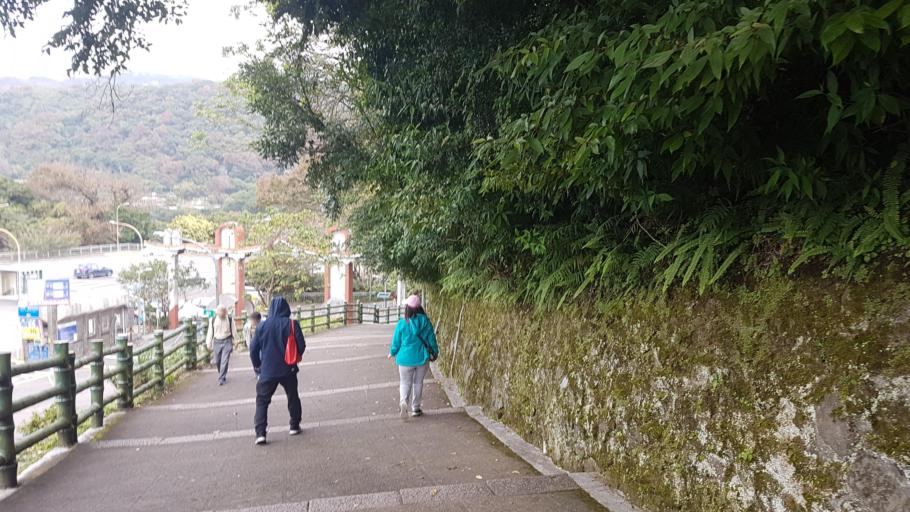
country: TW
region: Taipei
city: Taipei
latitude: 25.1542
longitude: 121.5392
